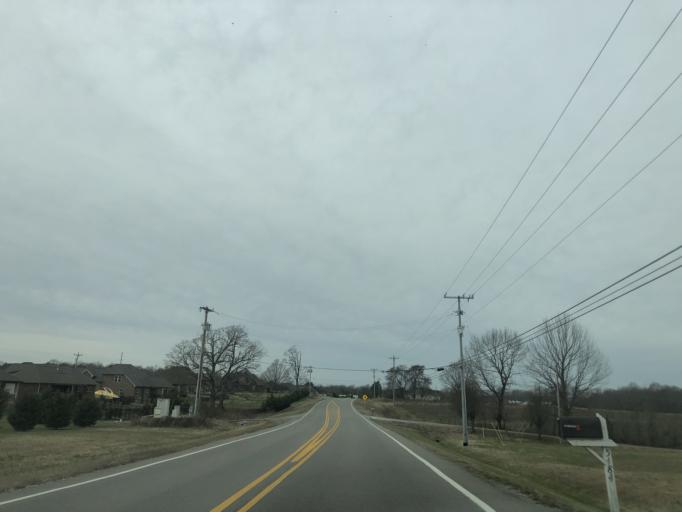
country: US
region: Tennessee
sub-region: Robertson County
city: Greenbrier
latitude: 36.4025
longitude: -86.8158
